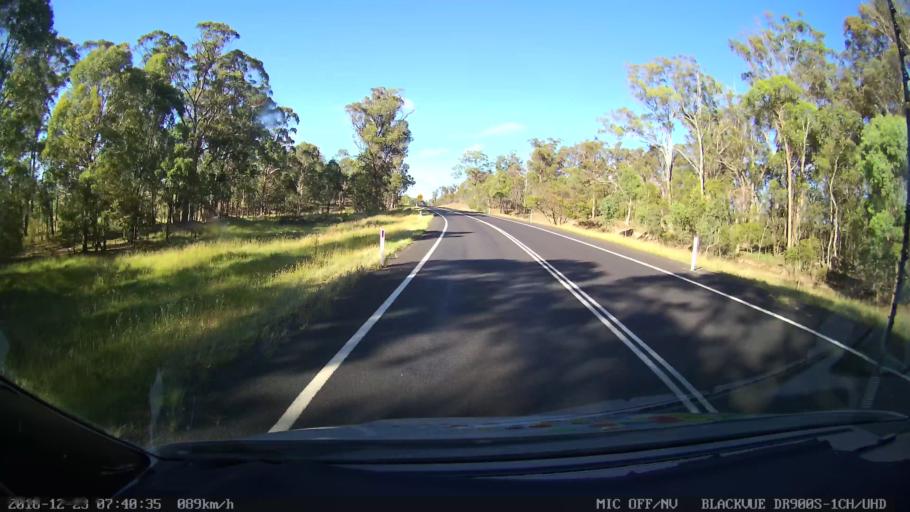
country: AU
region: New South Wales
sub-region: Armidale Dumaresq
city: Enmore
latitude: -30.5145
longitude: 152.0048
